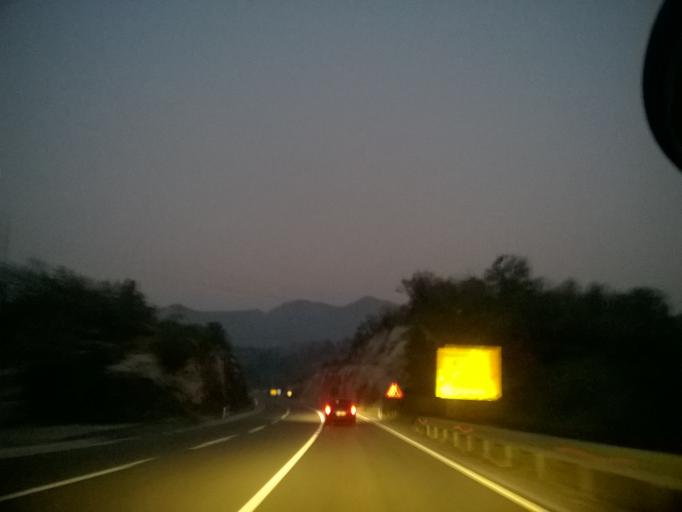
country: ME
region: Cetinje
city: Cetinje
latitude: 42.3777
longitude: 18.9884
